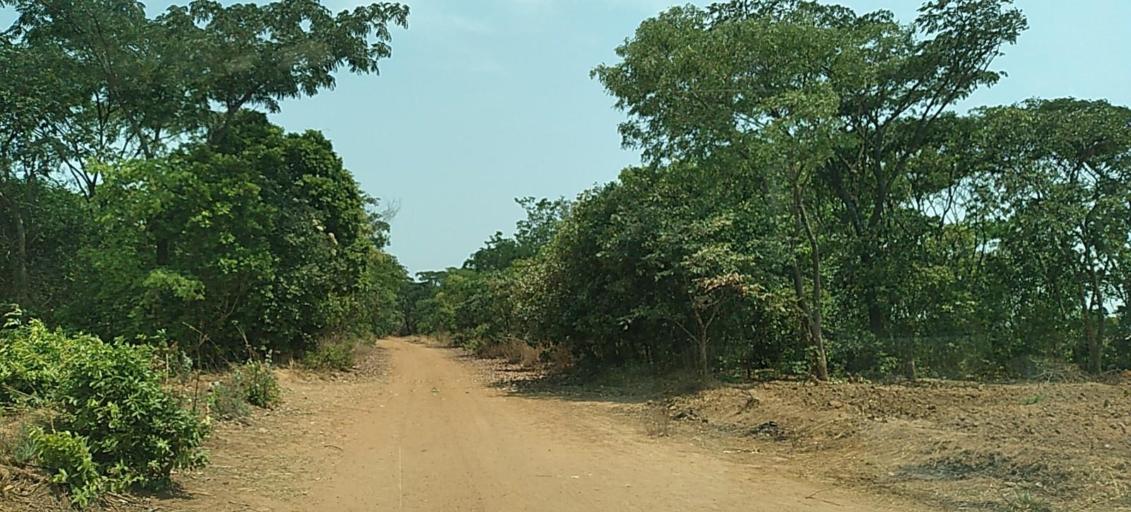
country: ZM
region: Copperbelt
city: Ndola
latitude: -13.0502
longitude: 28.7374
